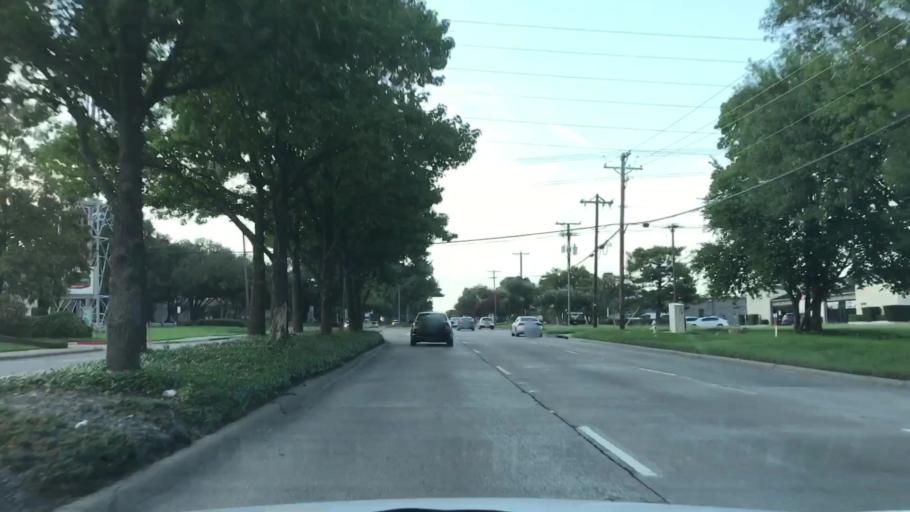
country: US
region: Texas
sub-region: Dallas County
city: Addison
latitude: 32.9463
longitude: -96.8389
